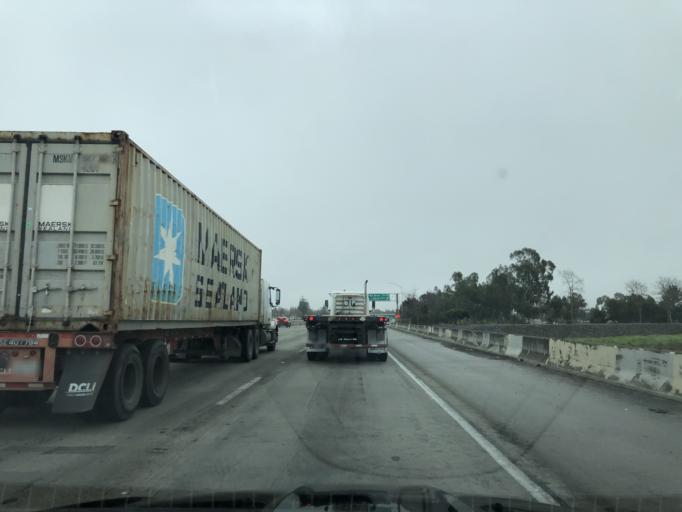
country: US
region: California
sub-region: Alameda County
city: Union City
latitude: 37.5840
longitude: -122.0507
